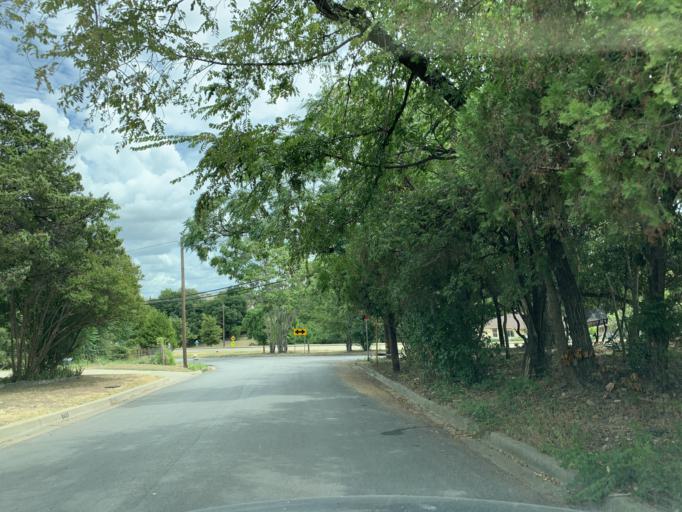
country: US
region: Texas
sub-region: Dallas County
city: Cockrell Hill
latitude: 32.7422
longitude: -96.8763
